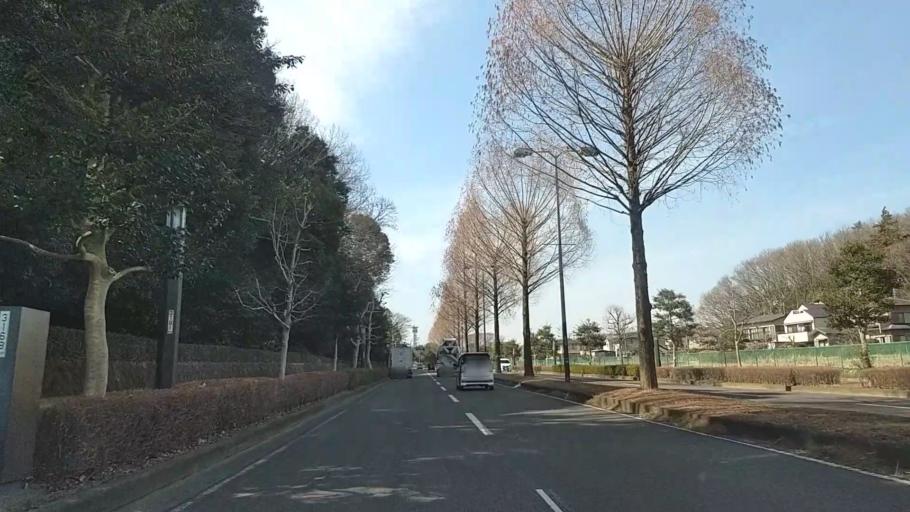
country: JP
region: Kanagawa
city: Fujisawa
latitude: 35.3913
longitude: 139.4279
